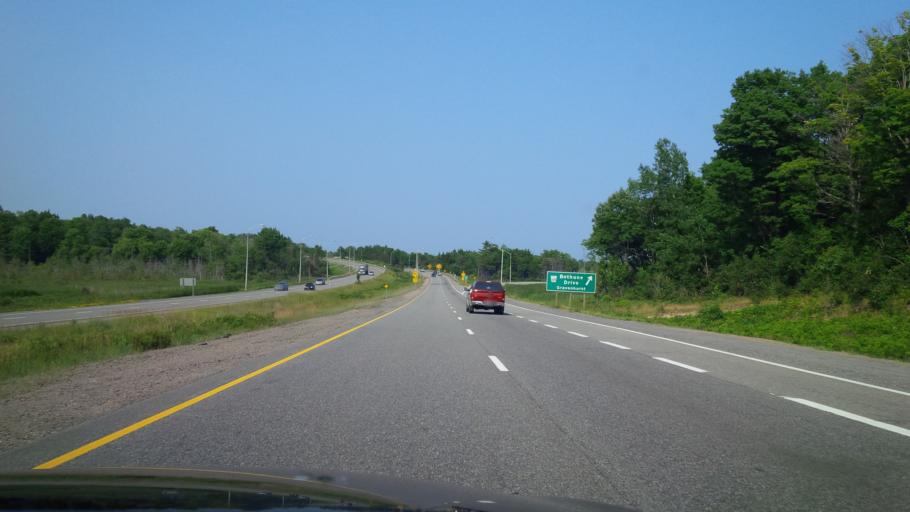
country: CA
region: Ontario
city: Gravenhurst
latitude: 44.9078
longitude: -79.3593
